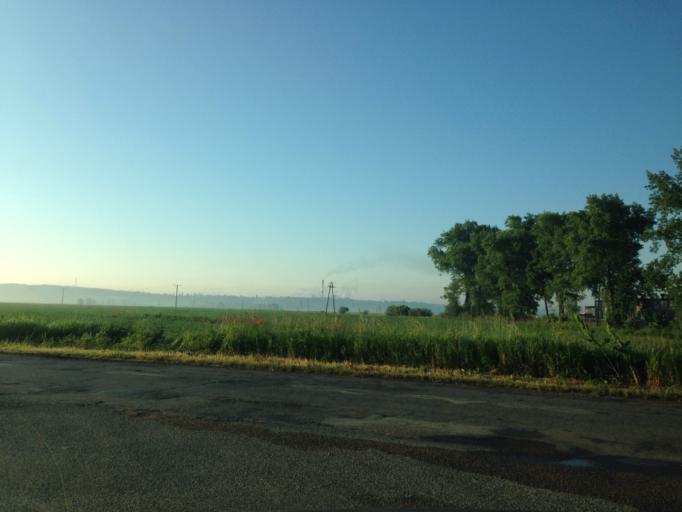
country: PL
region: Pomeranian Voivodeship
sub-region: Powiat kwidzynski
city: Kwidzyn
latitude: 53.7269
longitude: 18.8795
